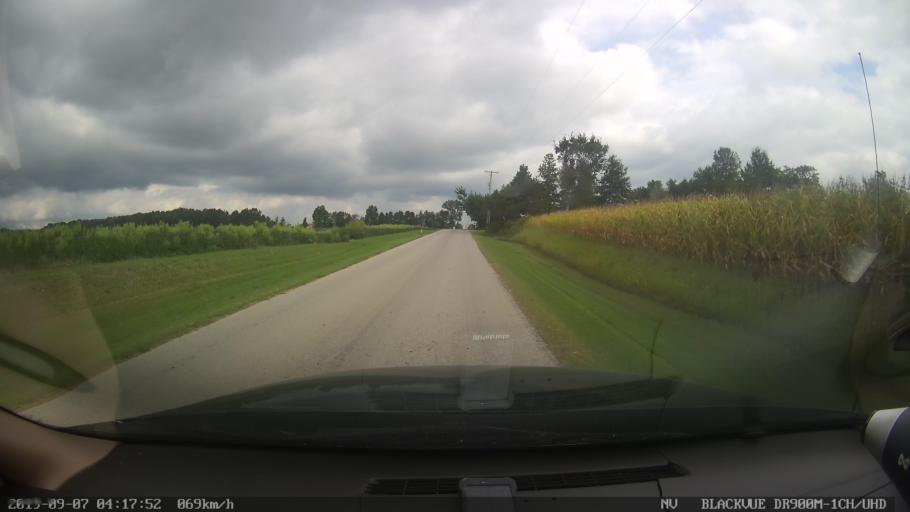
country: US
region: Ohio
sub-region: Knox County
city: Centerburg
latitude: 40.2492
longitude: -82.6638
